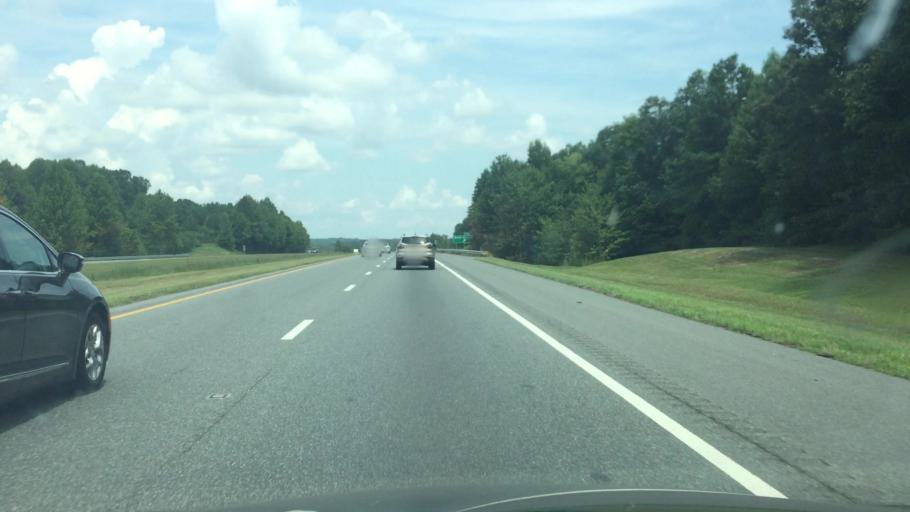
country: US
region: North Carolina
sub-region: Montgomery County
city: Biscoe
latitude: 35.4818
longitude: -79.7817
